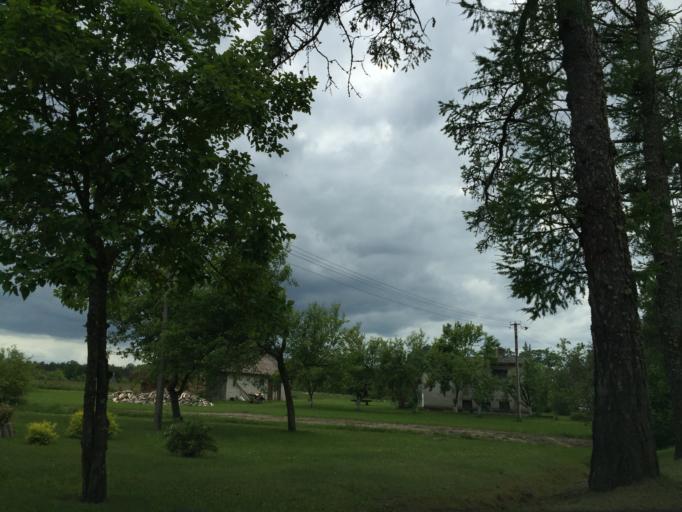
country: LV
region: Apes Novads
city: Ape
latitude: 57.4223
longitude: 26.3619
